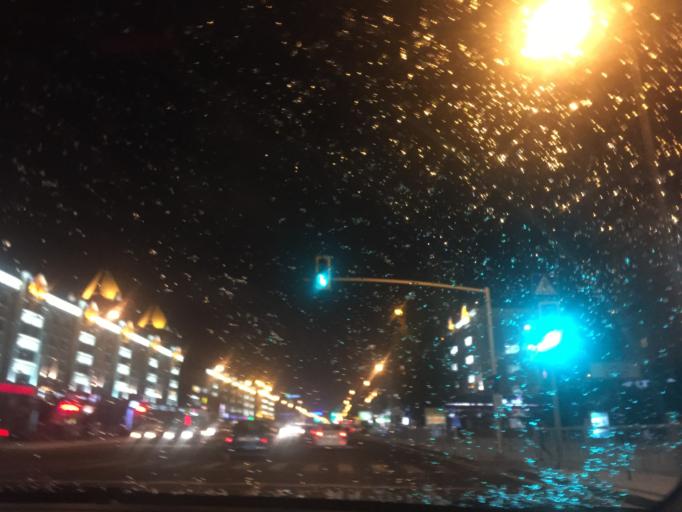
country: KZ
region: Astana Qalasy
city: Astana
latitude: 51.1584
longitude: 71.4295
